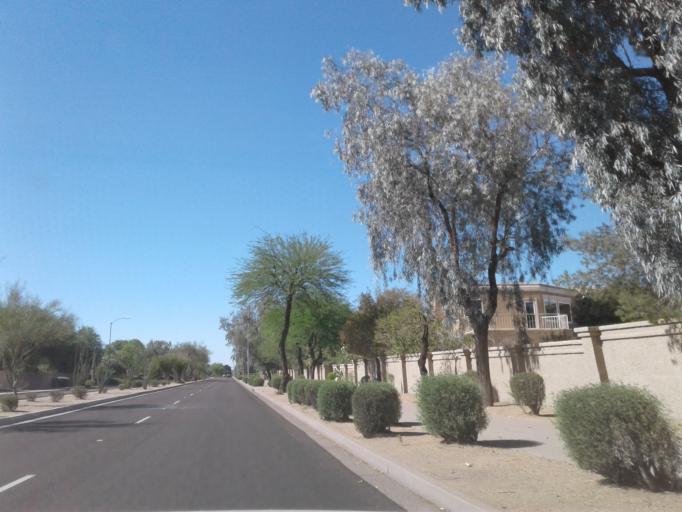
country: US
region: Arizona
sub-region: Maricopa County
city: Scottsdale
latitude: 33.6032
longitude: -111.8785
